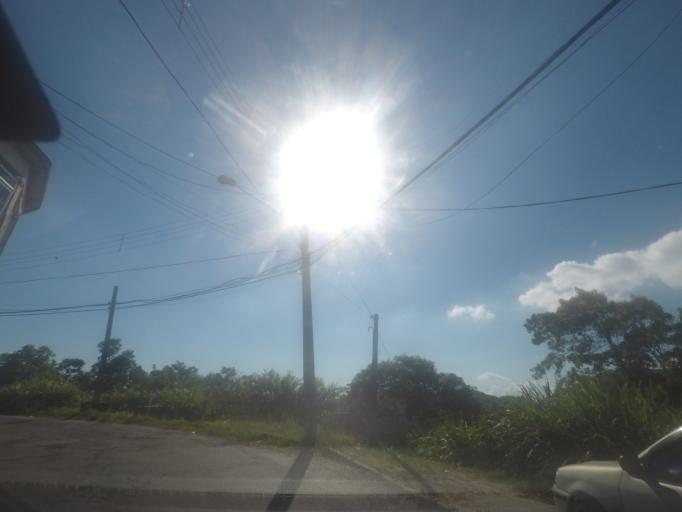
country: BR
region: Rio de Janeiro
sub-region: Petropolis
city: Petropolis
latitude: -22.5455
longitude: -43.2038
